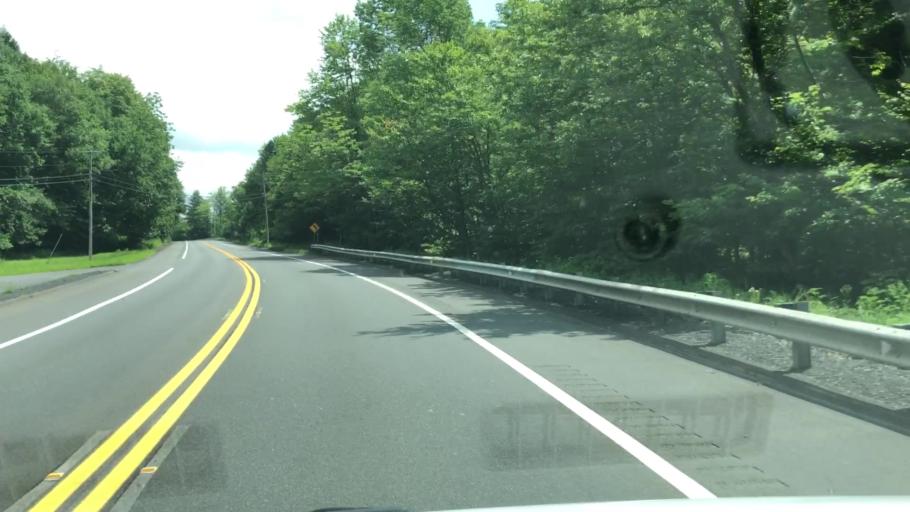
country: US
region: Massachusetts
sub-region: Hampshire County
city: Chesterfield
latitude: 42.4496
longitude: -72.8205
